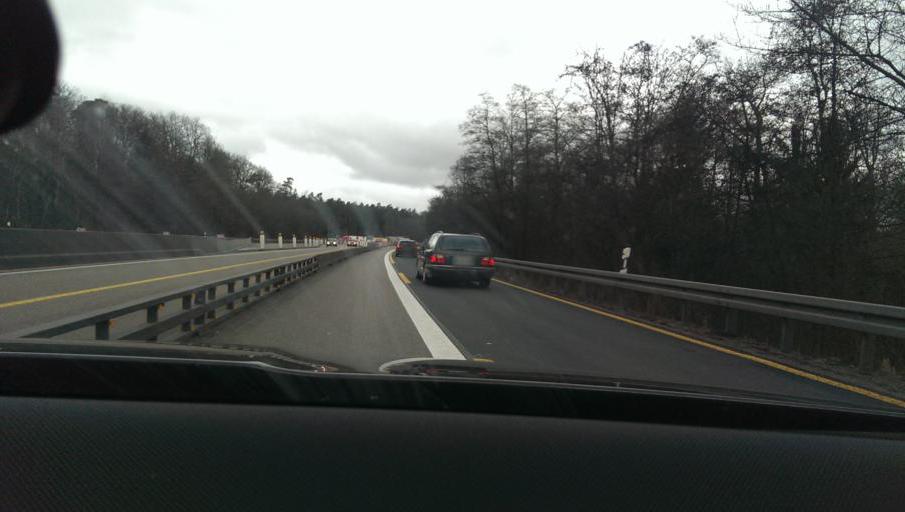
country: DE
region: Hesse
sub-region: Regierungsbezirk Kassel
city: Fulda
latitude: 50.6025
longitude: 9.6806
